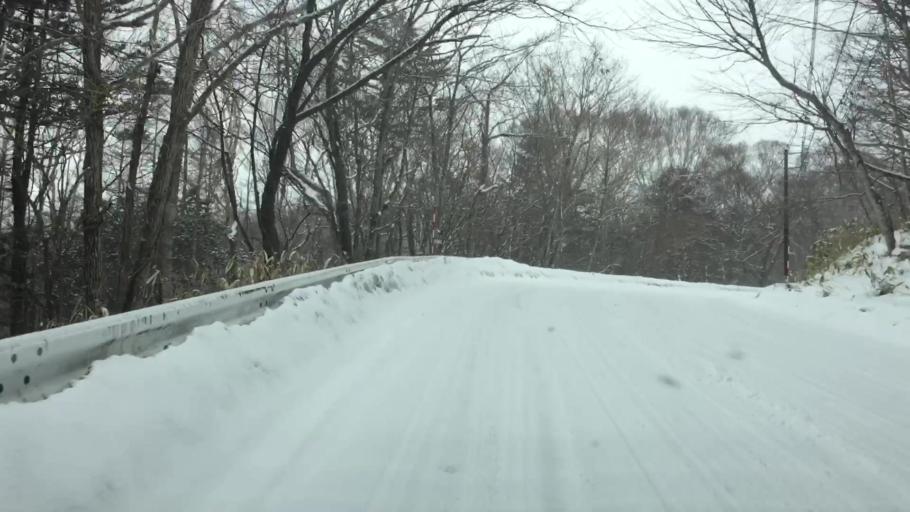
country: JP
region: Tochigi
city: Nikko
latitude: 36.9109
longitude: 139.7374
